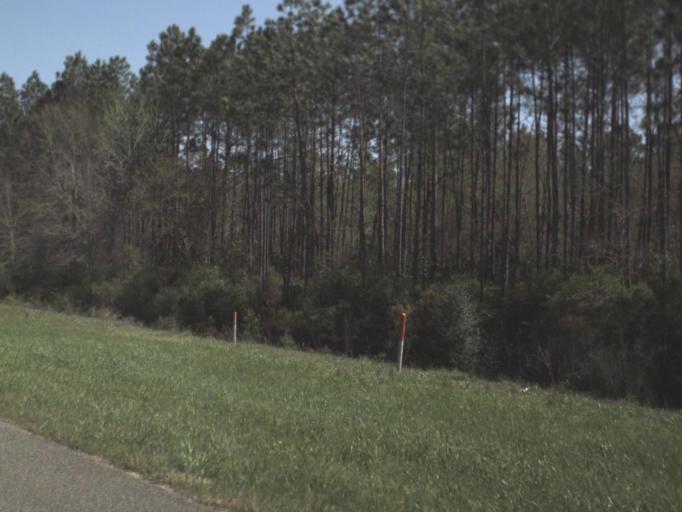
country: US
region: Florida
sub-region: Calhoun County
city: Blountstown
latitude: 30.4257
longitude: -85.1218
